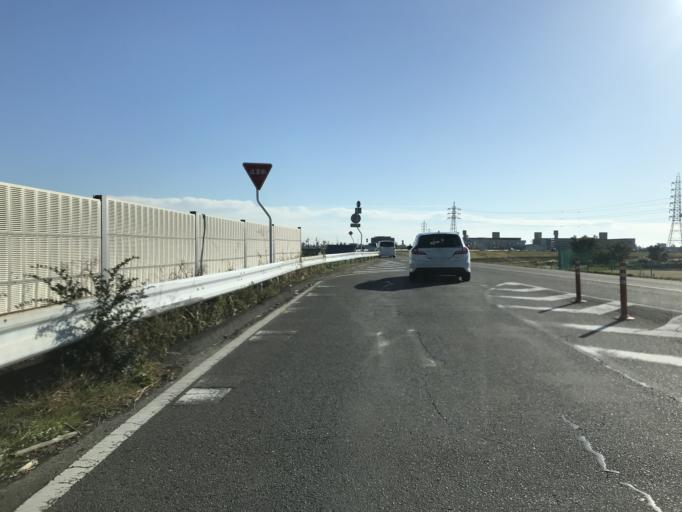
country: JP
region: Aichi
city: Kanie
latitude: 35.1558
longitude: 136.8399
